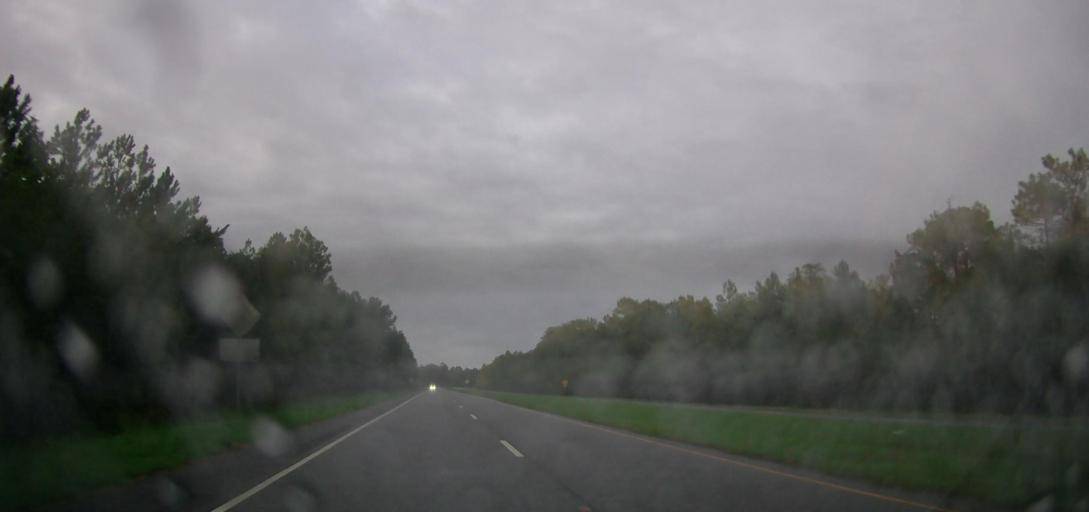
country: US
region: Georgia
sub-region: Clinch County
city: Homerville
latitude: 30.9953
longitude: -82.8656
